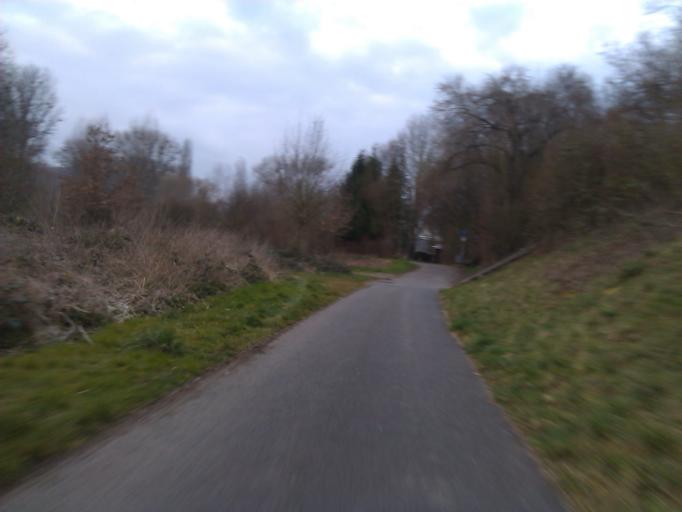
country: DE
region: Rheinland-Pfalz
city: Rhens
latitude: 50.2826
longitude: 7.6275
